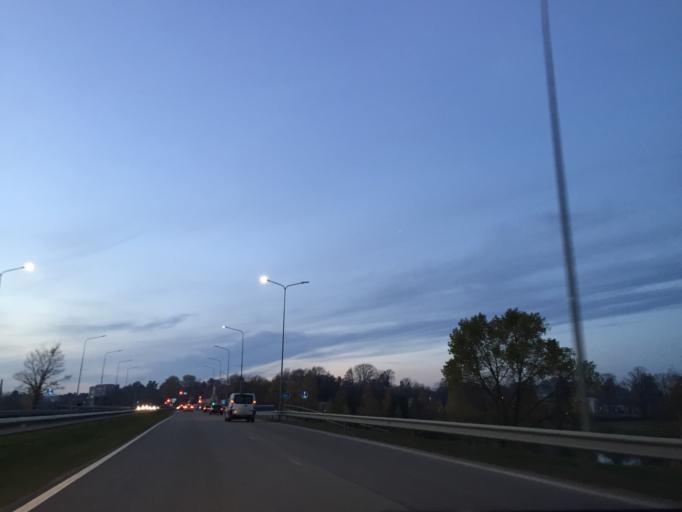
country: LV
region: Ogre
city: Ogre
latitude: 56.8098
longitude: 24.6021
